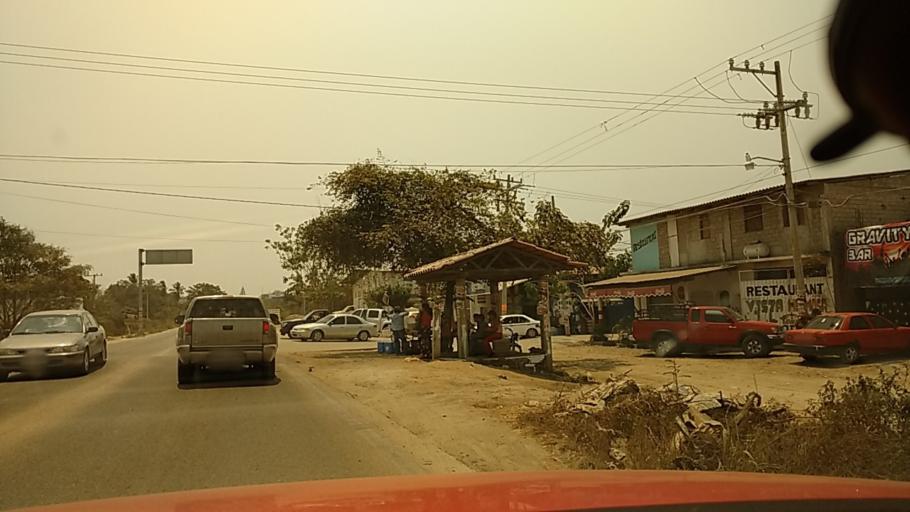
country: MX
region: Guerrero
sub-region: Tecpan de Galeana
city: Villa Rotaria
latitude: 17.2711
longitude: -100.8868
